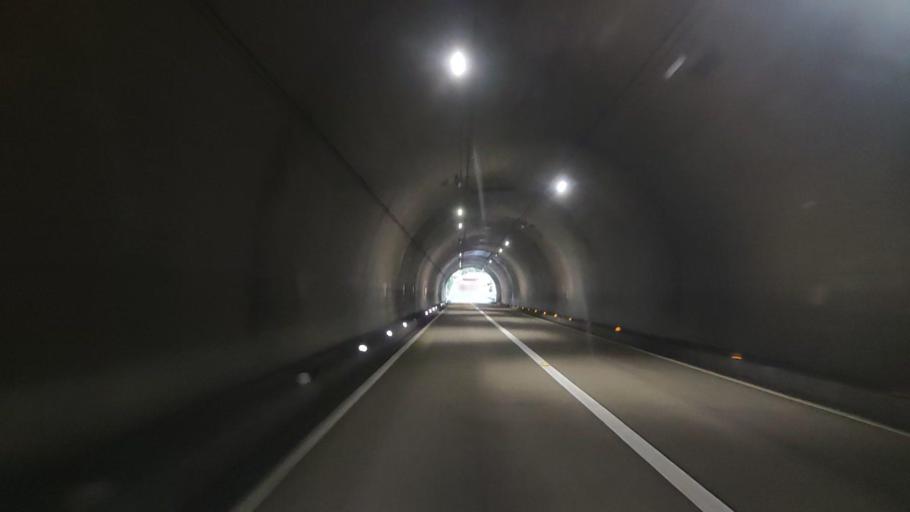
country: JP
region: Wakayama
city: Shingu
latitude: 33.8075
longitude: 135.7102
